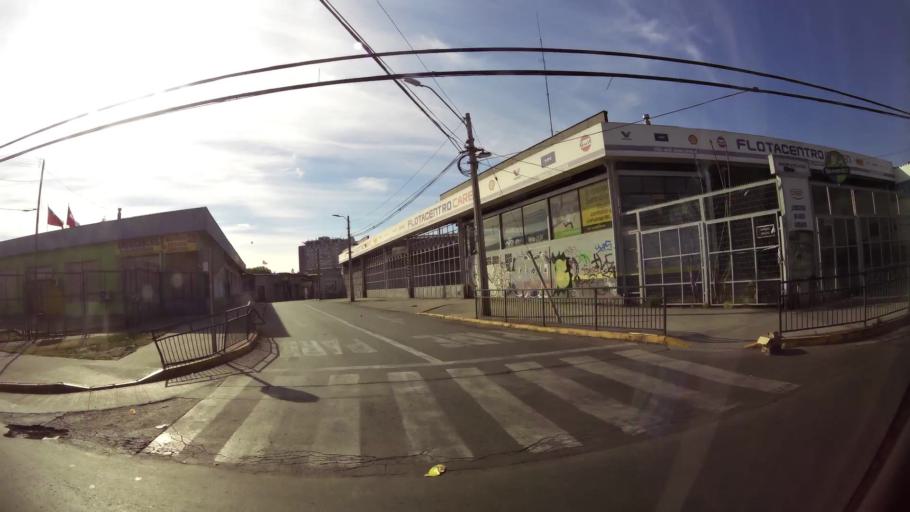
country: CL
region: Santiago Metropolitan
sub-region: Provincia de Santiago
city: Santiago
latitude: -33.4548
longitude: -70.6822
